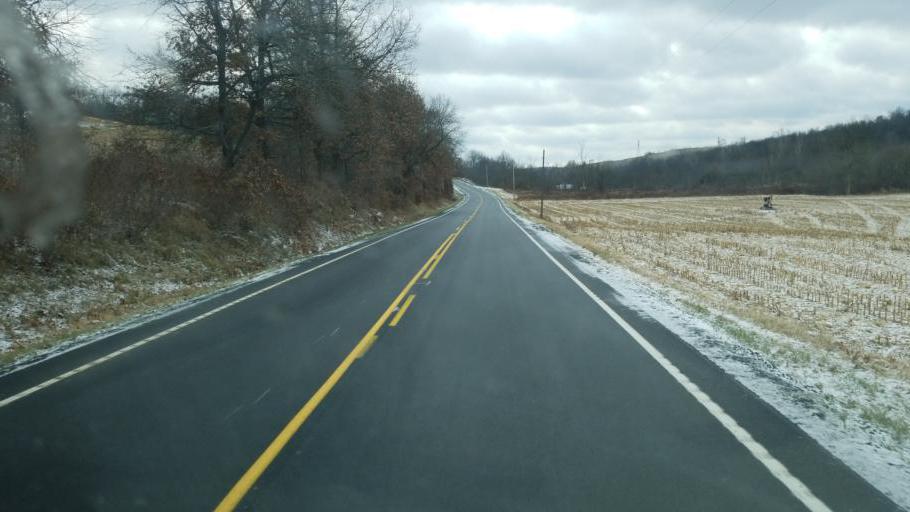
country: US
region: Ohio
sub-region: Muskingum County
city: Frazeysburg
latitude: 40.1501
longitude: -82.2173
